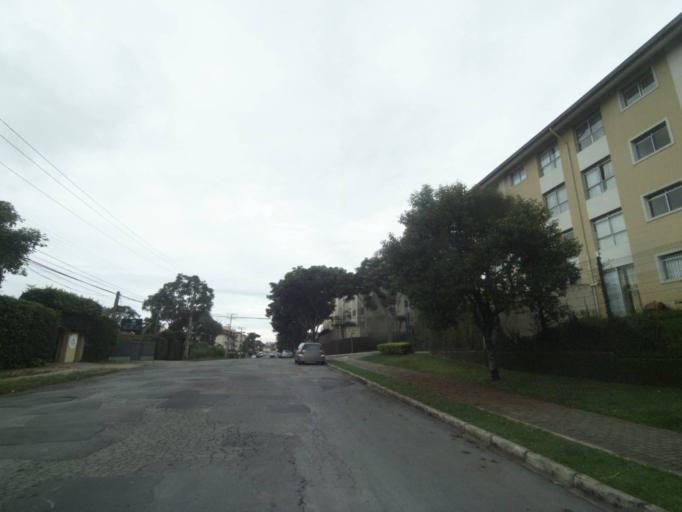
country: BR
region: Parana
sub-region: Curitiba
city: Curitiba
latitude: -25.4581
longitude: -49.3253
